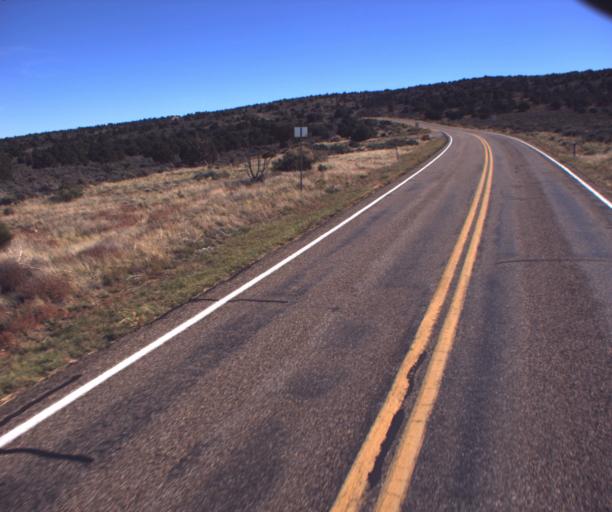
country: US
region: Arizona
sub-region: Coconino County
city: Fredonia
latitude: 36.8452
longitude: -112.2794
